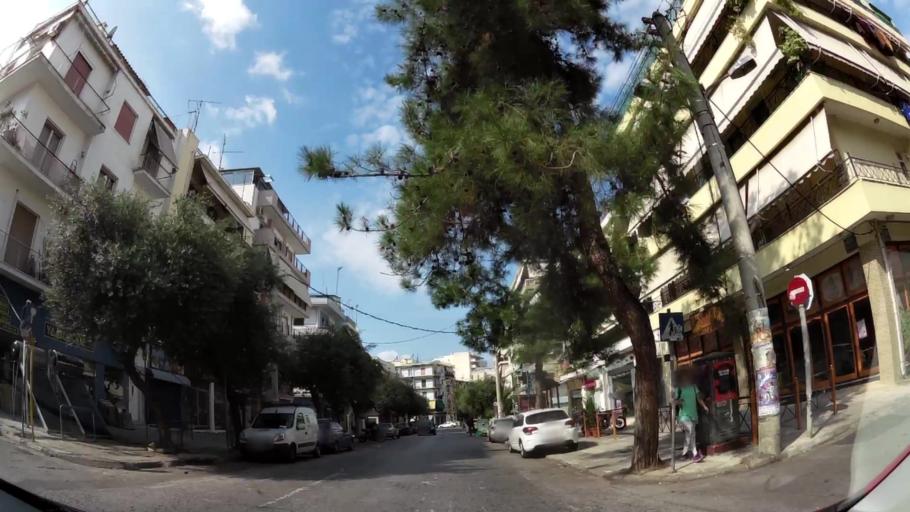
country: GR
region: Attica
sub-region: Nomarchia Athinas
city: Nea Smyrni
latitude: 37.9543
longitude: 23.7219
